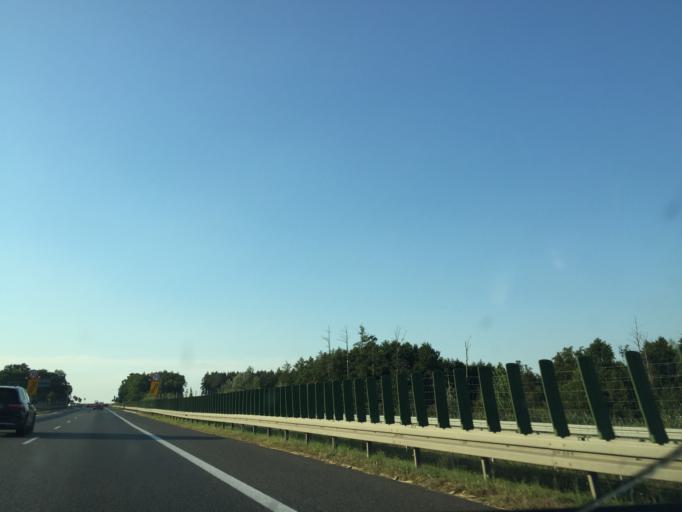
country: PL
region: Masovian Voivodeship
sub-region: Powiat grojecki
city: Grojec
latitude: 51.9031
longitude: 20.8590
